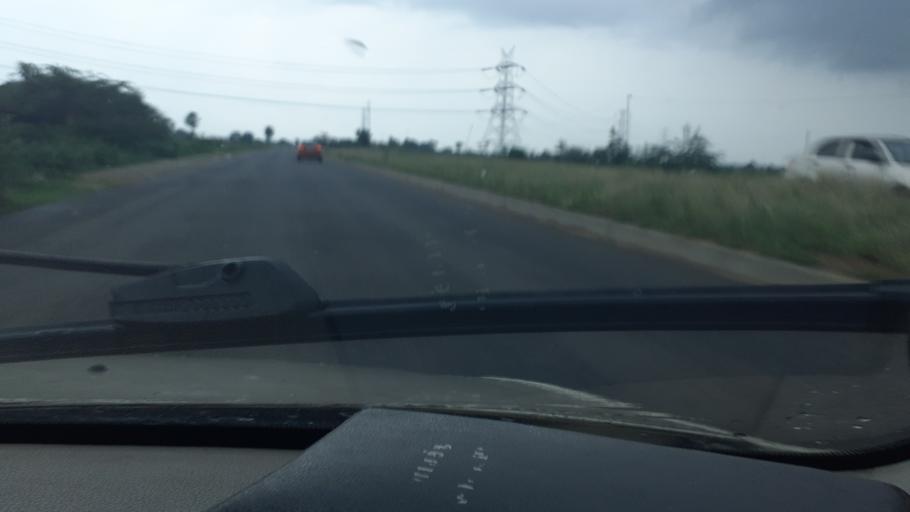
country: IN
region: Tamil Nadu
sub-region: Thoothukkudi
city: Kadambur
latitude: 9.0714
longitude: 77.7994
